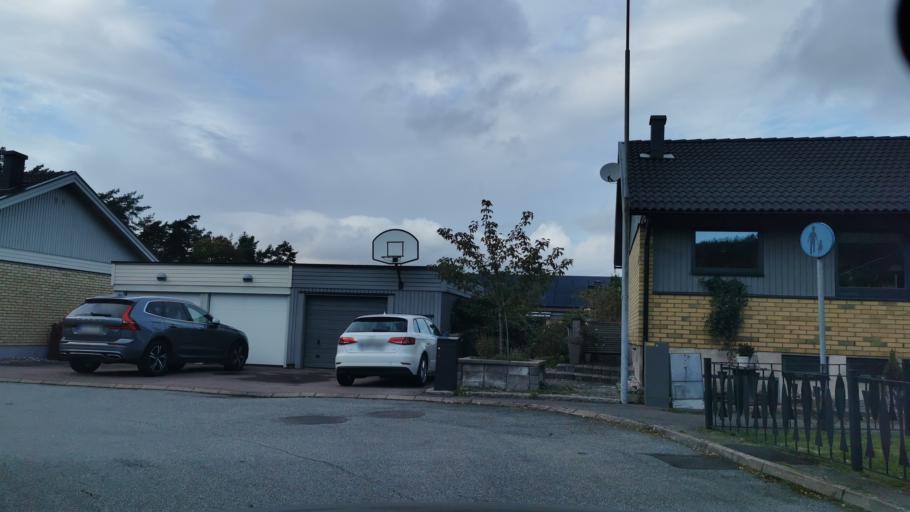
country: SE
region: Vaestra Goetaland
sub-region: Partille Kommun
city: Partille
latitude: 57.7138
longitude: 12.0755
